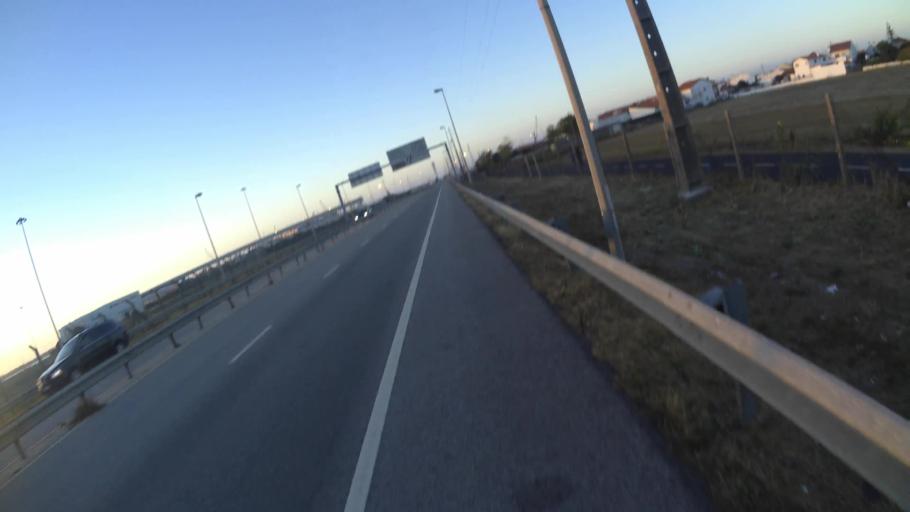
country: PT
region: Aveiro
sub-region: Ilhavo
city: Gafanha da Nazare
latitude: 40.6358
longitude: -8.7279
